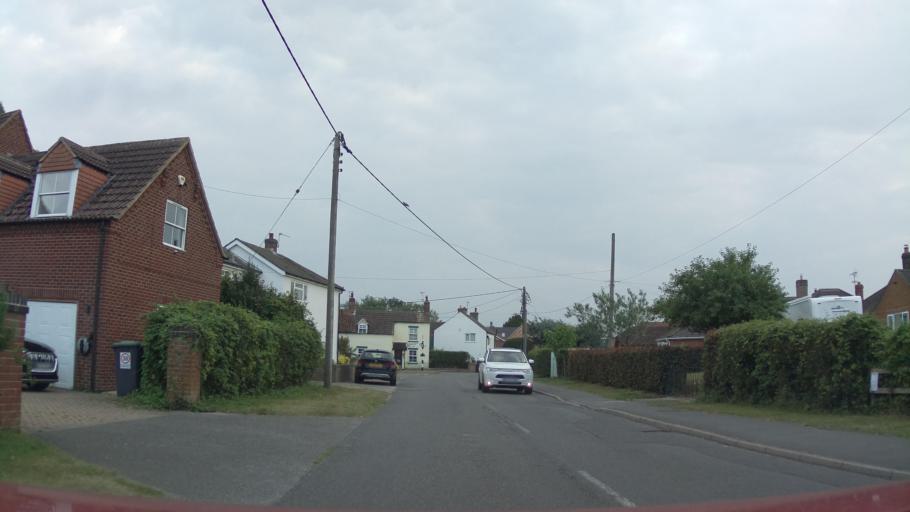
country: GB
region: England
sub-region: Lincolnshire
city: Skellingthorpe
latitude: 53.1323
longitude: -0.6381
